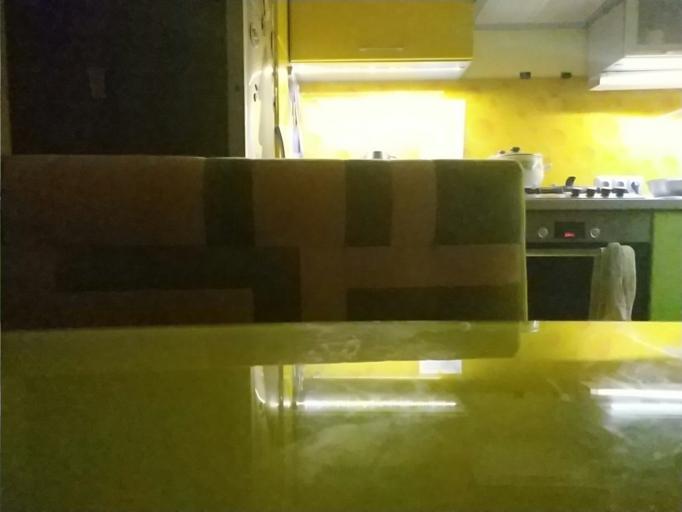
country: RU
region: Republic of Karelia
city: Pyaozerskiy
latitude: 65.7802
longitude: 30.4820
